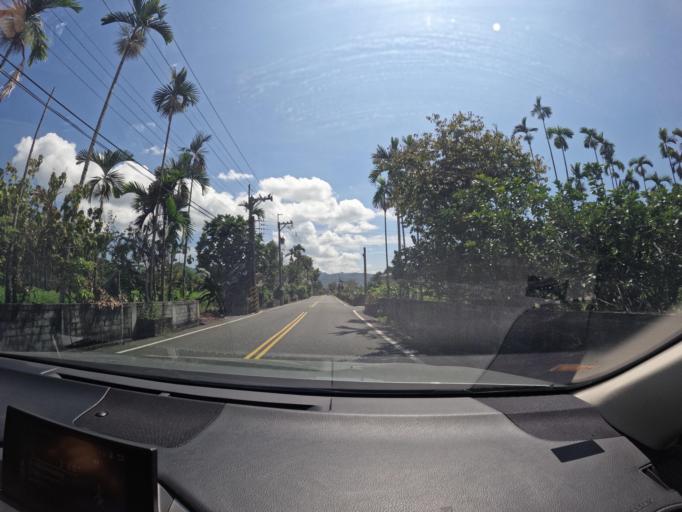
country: TW
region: Taiwan
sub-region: Hualien
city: Hualian
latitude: 23.5813
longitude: 121.3688
